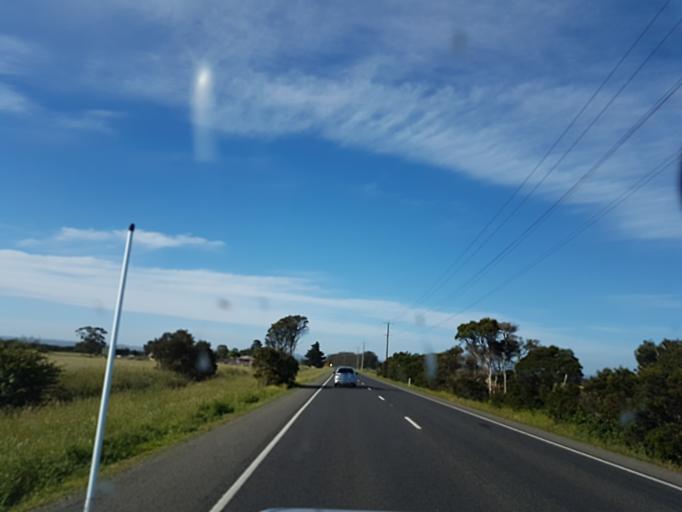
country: AU
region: Victoria
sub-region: Cardinia
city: Pakenham South
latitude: -38.1429
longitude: 145.4879
